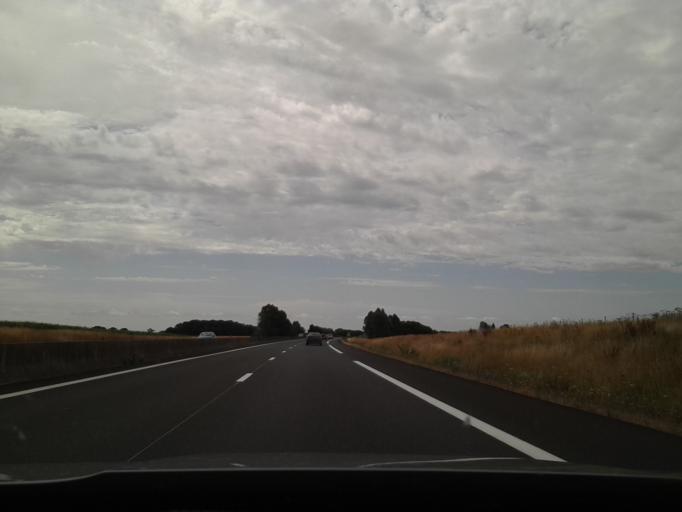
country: FR
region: Pays de la Loire
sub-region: Departement de la Sarthe
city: Beaumont-sur-Sarthe
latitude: 48.2730
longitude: 0.1601
